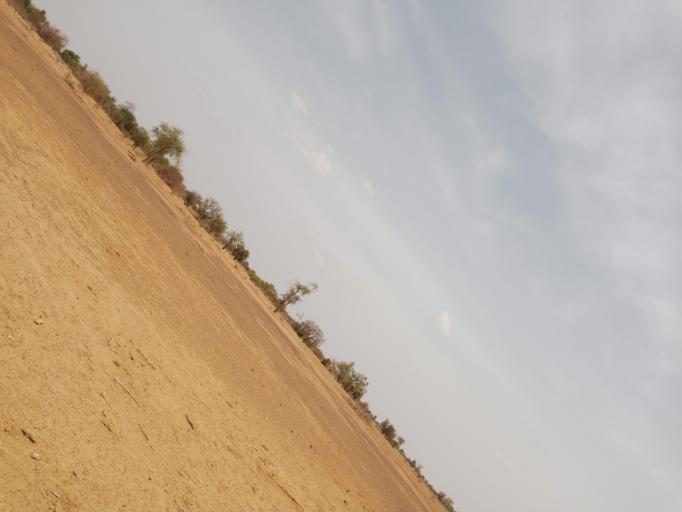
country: BF
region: Est
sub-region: Gnagna Province
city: Bogande
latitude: 13.0969
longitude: -0.0400
